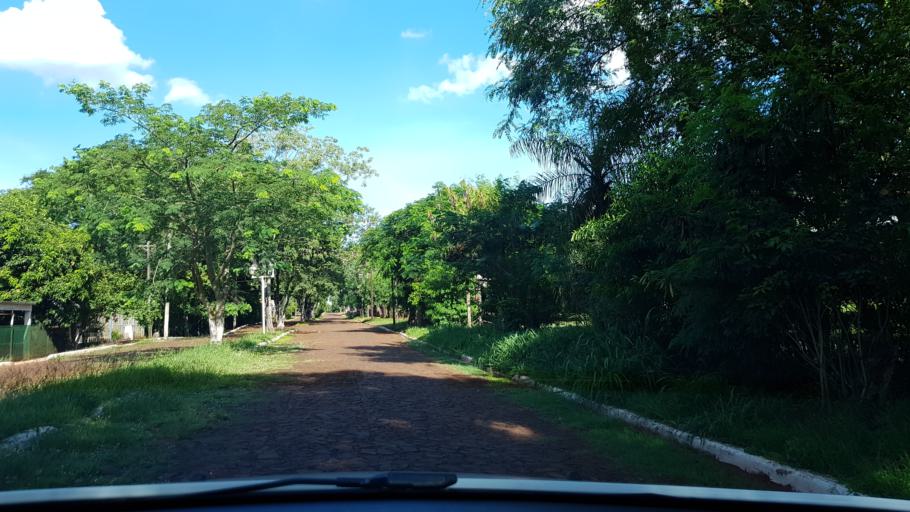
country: AR
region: Misiones
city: Puerto Libertad
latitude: -25.9217
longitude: -54.5879
